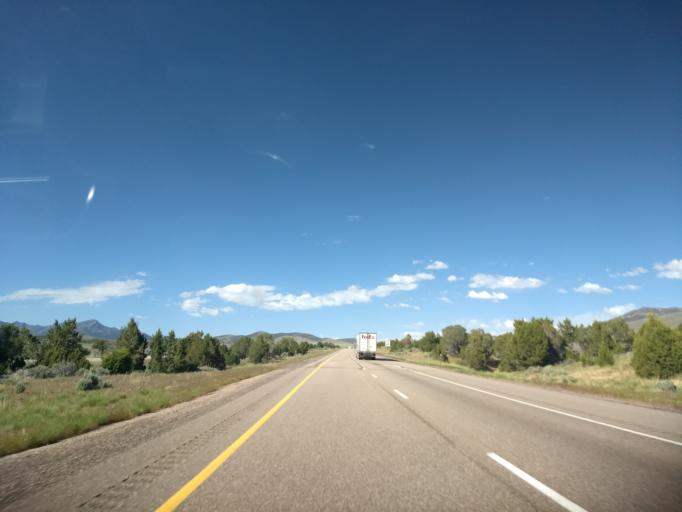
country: US
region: Utah
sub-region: Millard County
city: Fillmore
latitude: 39.1539
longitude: -112.2290
